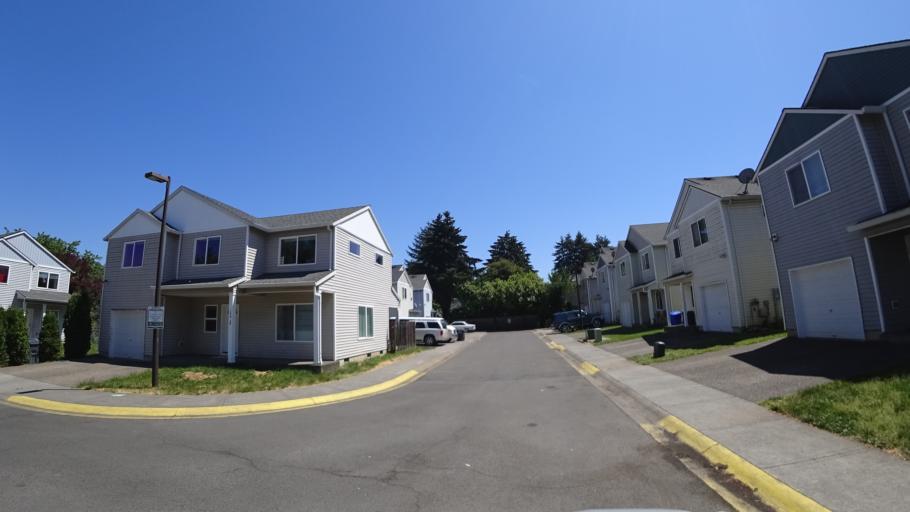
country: US
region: Oregon
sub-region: Clackamas County
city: Happy Valley
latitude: 45.4794
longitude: -122.5336
